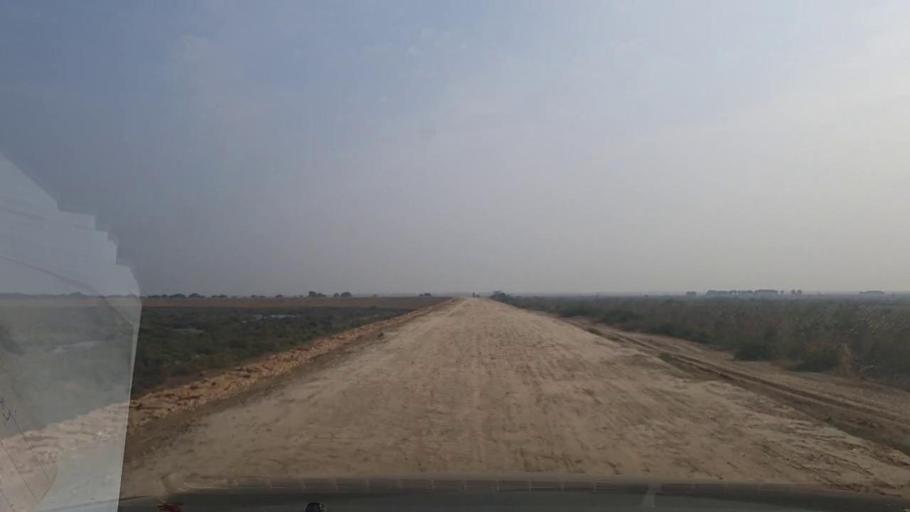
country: PK
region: Sindh
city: Bulri
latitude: 24.9453
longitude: 68.2856
